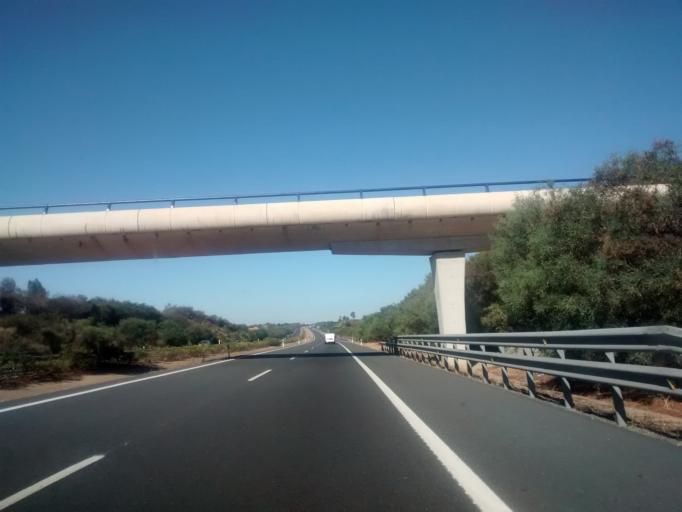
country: ES
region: Andalusia
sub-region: Provincia de Huelva
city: Lepe
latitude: 37.2665
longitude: -7.2762
